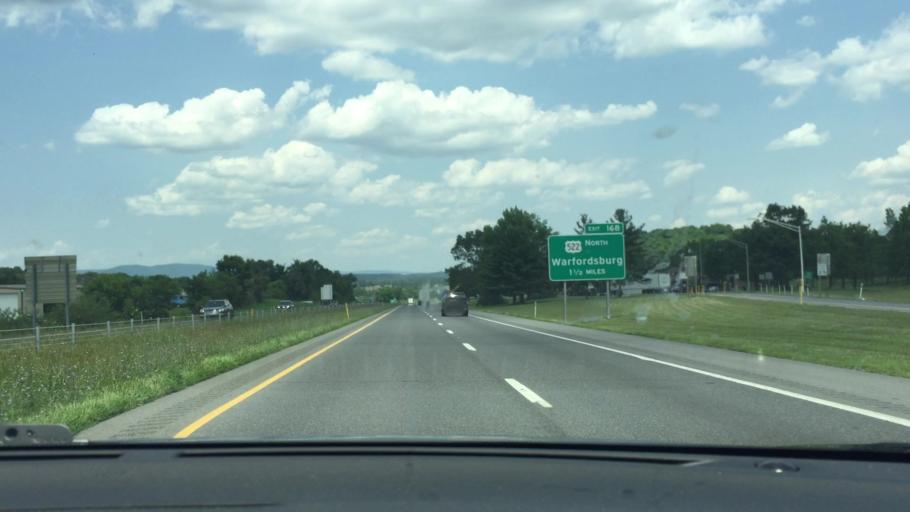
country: US
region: Maryland
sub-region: Washington County
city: Hancock
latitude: 39.7350
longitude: -78.1818
